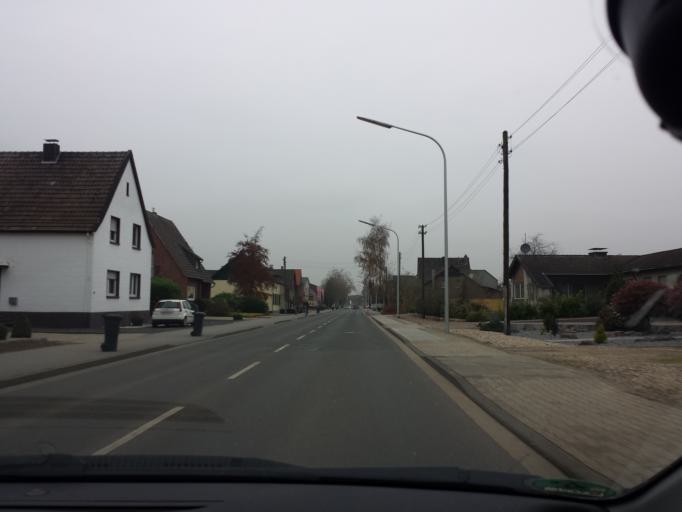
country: NL
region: Limburg
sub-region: Gemeente Roerdalen
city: Vlodrop
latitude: 51.0993
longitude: 6.0765
